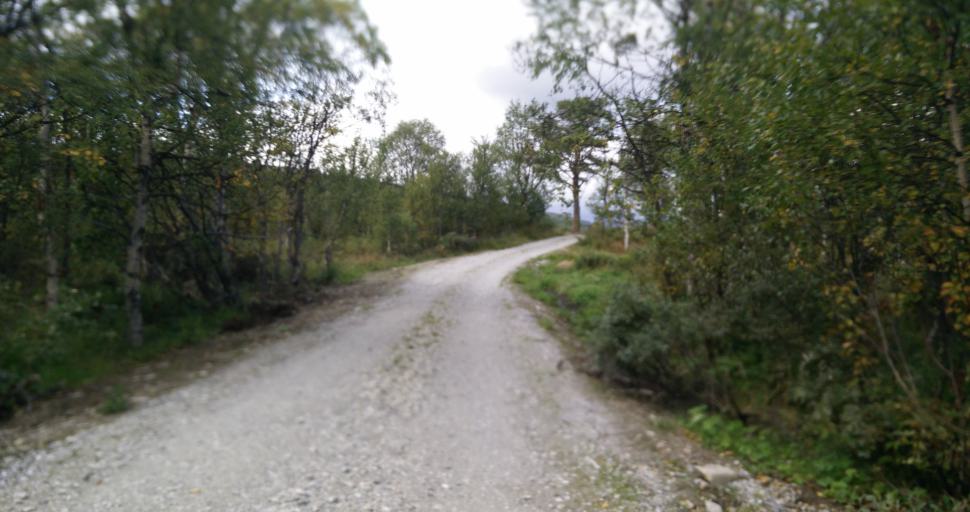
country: NO
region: Sor-Trondelag
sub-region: Tydal
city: Aas
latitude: 62.6385
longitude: 12.4175
